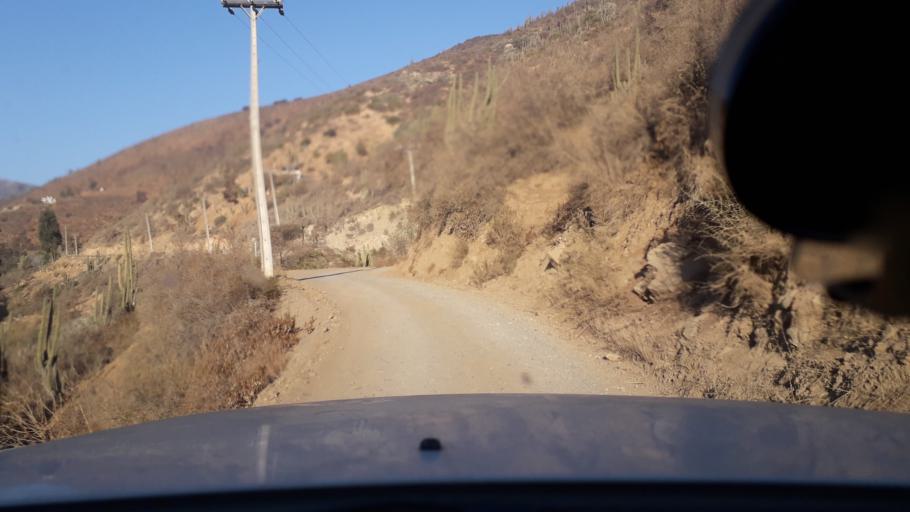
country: CL
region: Valparaiso
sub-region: Provincia de Marga Marga
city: Limache
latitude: -33.0522
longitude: -71.0749
